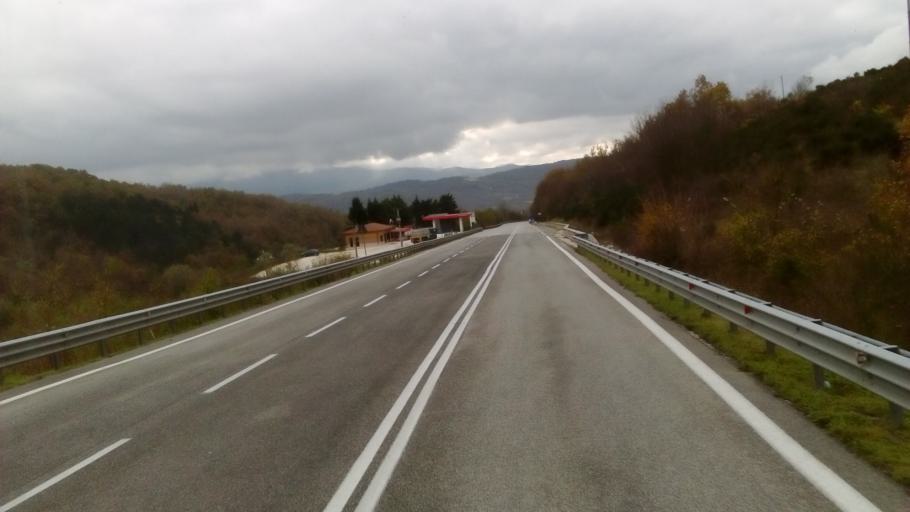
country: IT
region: Molise
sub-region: Provincia di Isernia
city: Sessano del Molise
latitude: 41.6516
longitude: 14.3334
